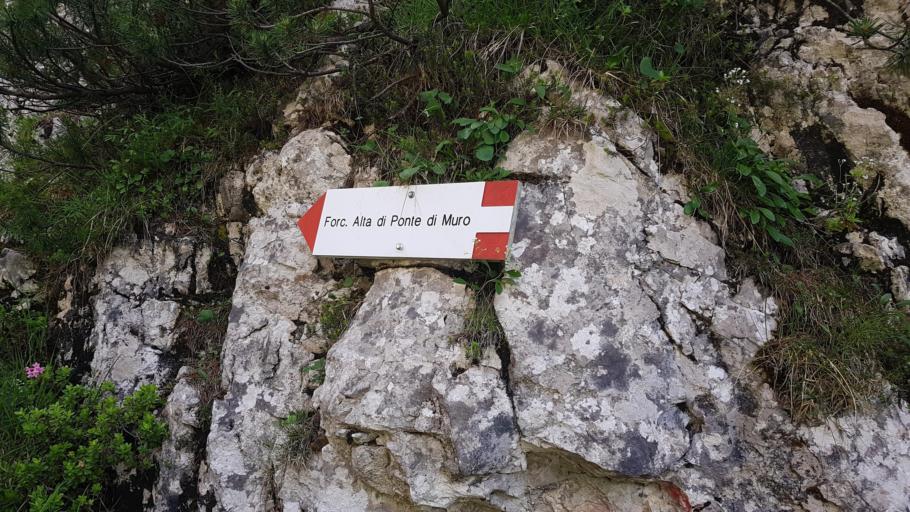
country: IT
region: Friuli Venezia Giulia
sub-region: Provincia di Udine
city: Pontebba
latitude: 46.4759
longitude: 13.2550
